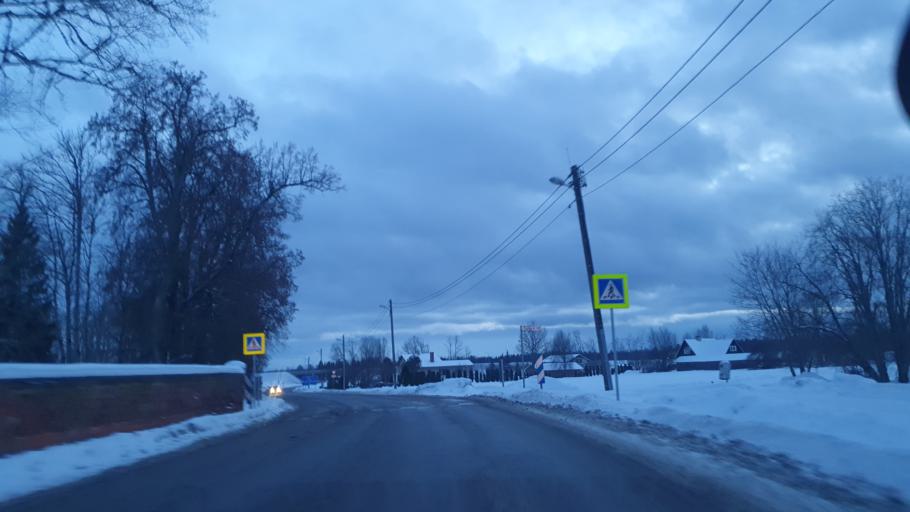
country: EE
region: Jogevamaa
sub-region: Jogeva linn
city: Jogeva
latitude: 58.5747
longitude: 26.2881
